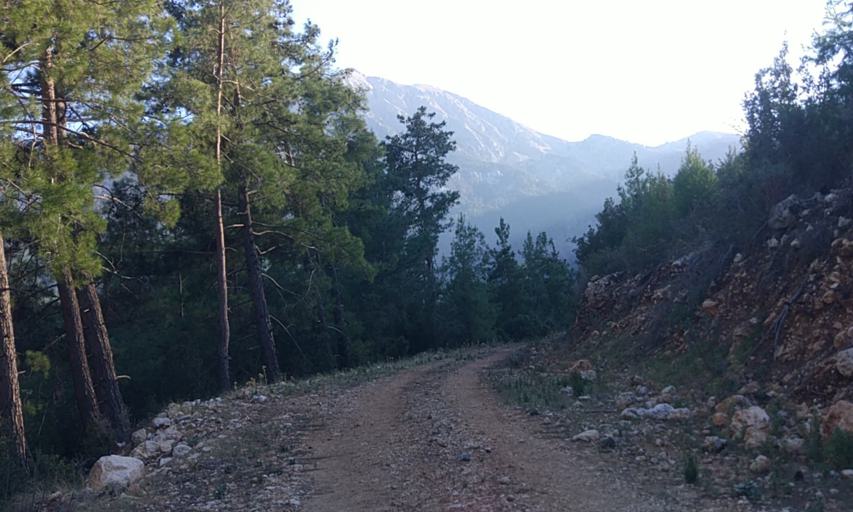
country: TR
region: Antalya
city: Altinyaka
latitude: 36.5910
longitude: 30.4268
